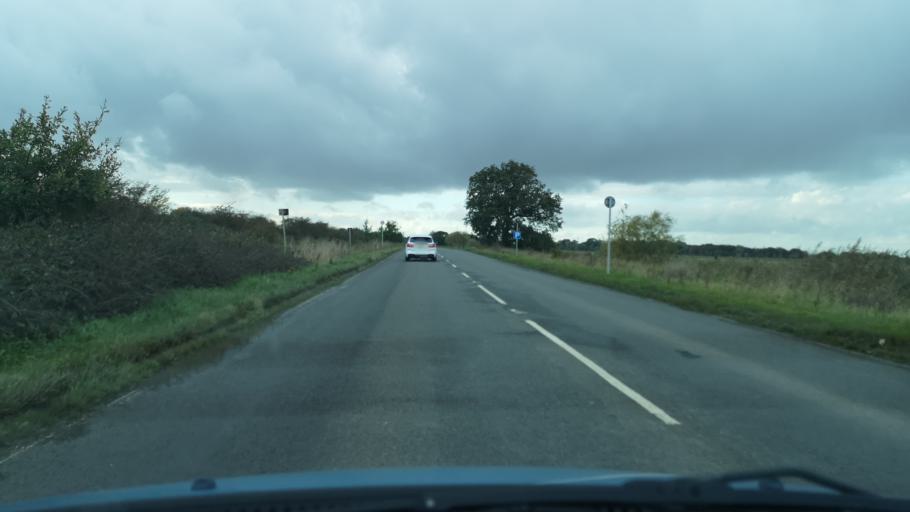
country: GB
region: England
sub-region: North Lincolnshire
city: Belton
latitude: 53.5810
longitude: -0.7921
